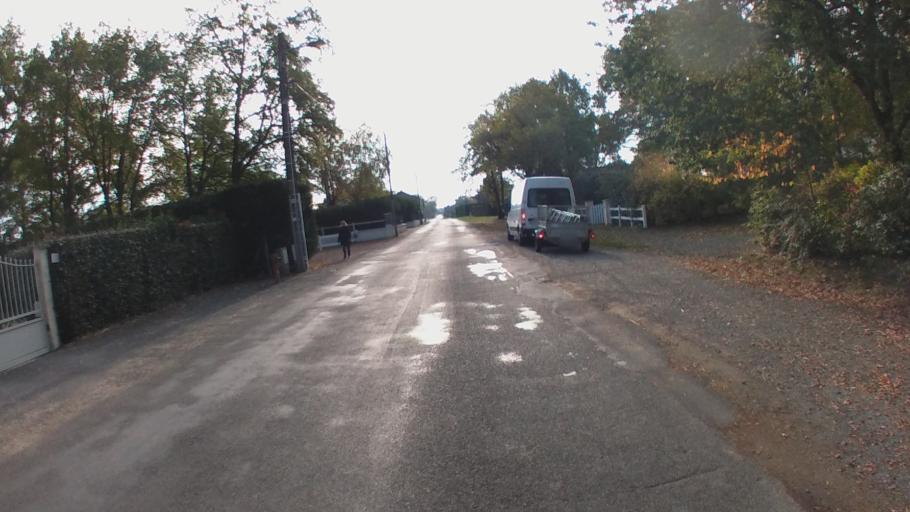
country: FR
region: Pays de la Loire
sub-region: Departement de Maine-et-Loire
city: Distre
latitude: 47.2514
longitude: -0.1116
